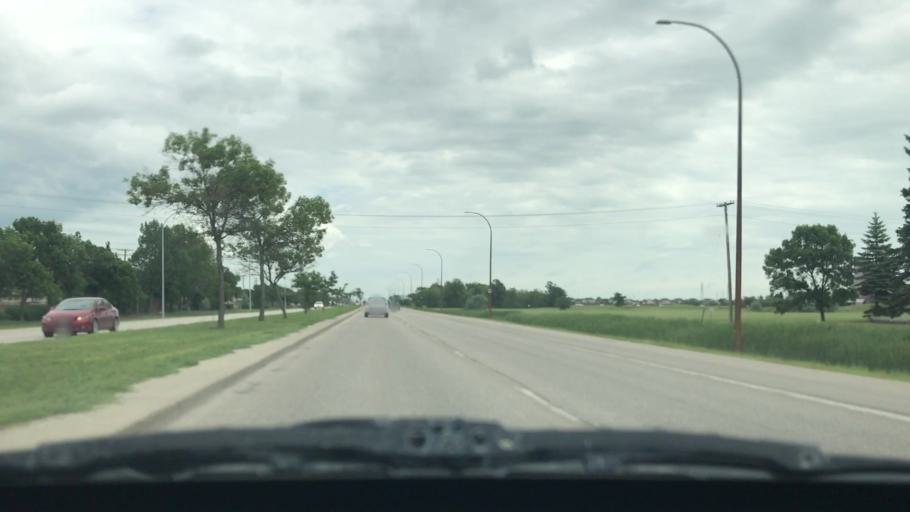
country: CA
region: Manitoba
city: Winnipeg
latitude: 49.8559
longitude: -97.0619
